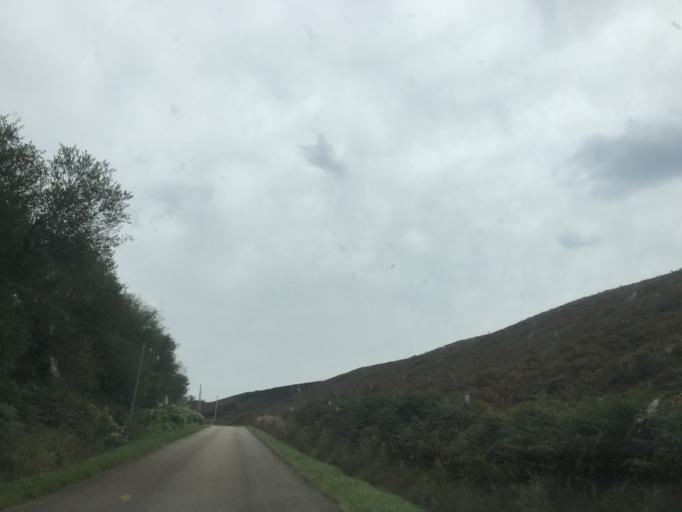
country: FR
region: Brittany
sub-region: Departement du Finistere
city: Brasparts
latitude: 48.3831
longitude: -3.9390
